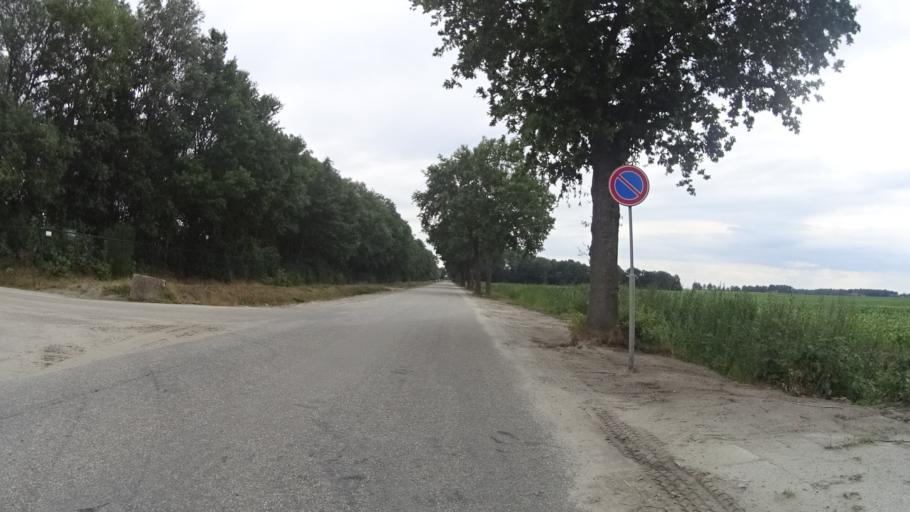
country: NL
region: Groningen
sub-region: Gemeente Slochteren
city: Slochteren
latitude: 53.1852
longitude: 6.8505
